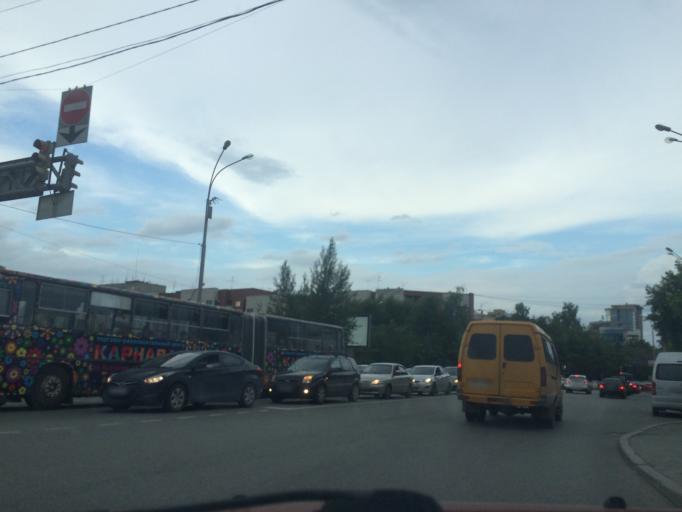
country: RU
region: Sverdlovsk
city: Yekaterinburg
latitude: 56.8177
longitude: 60.6070
